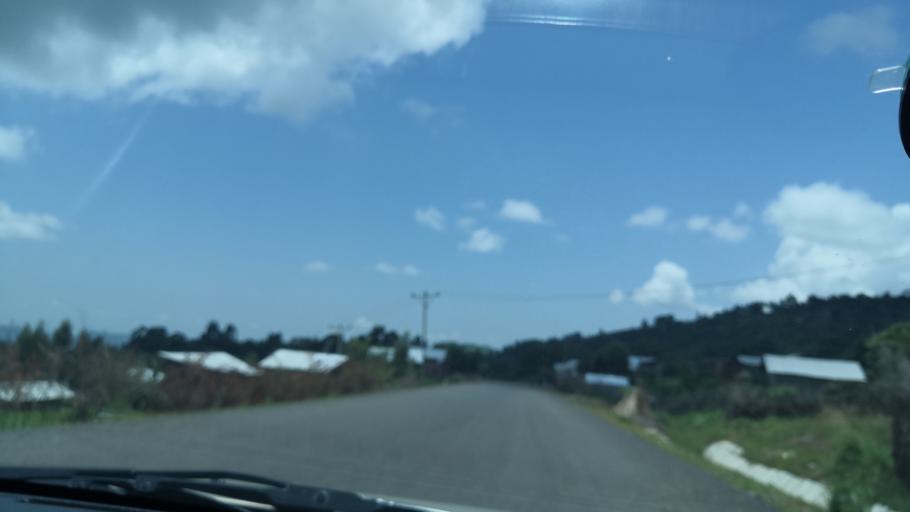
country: ET
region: Amhara
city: Abomsa
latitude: 10.3209
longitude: 39.8734
